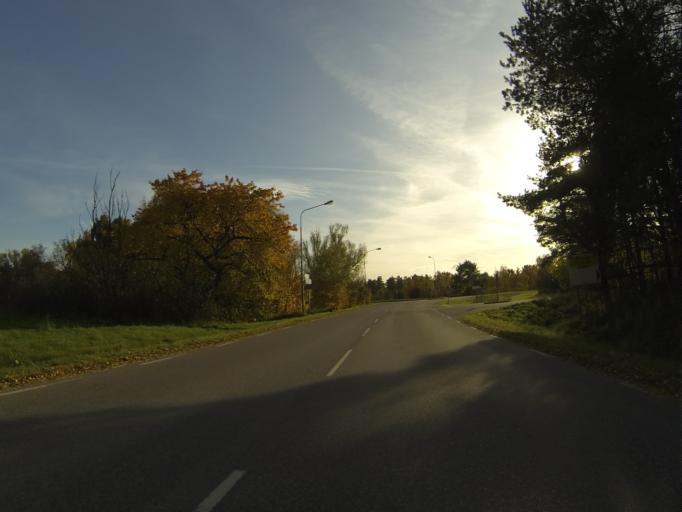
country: SE
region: Skane
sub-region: Hoors Kommun
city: Loberod
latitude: 55.7242
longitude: 13.4652
